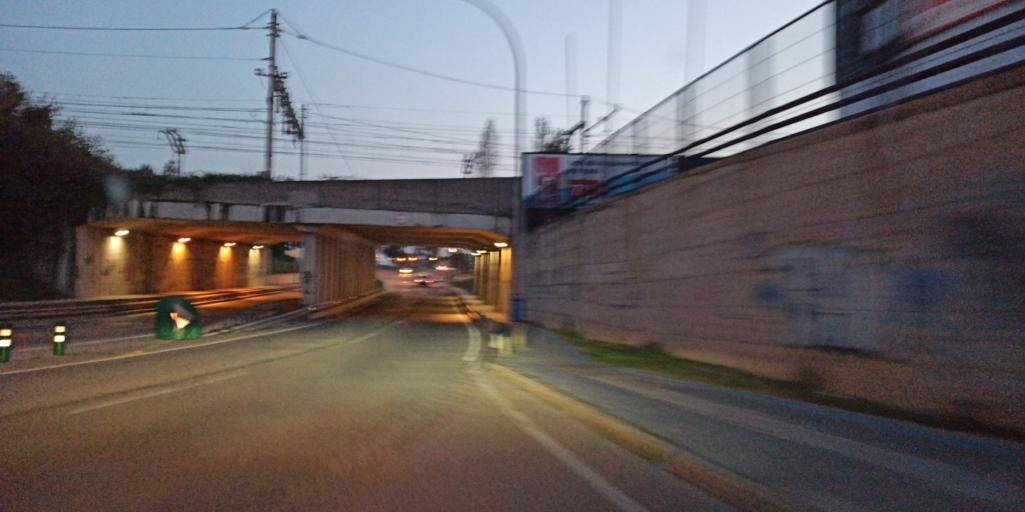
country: ES
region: Catalonia
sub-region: Provincia de Barcelona
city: Vilanova i la Geltru
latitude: 41.2202
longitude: 1.7372
